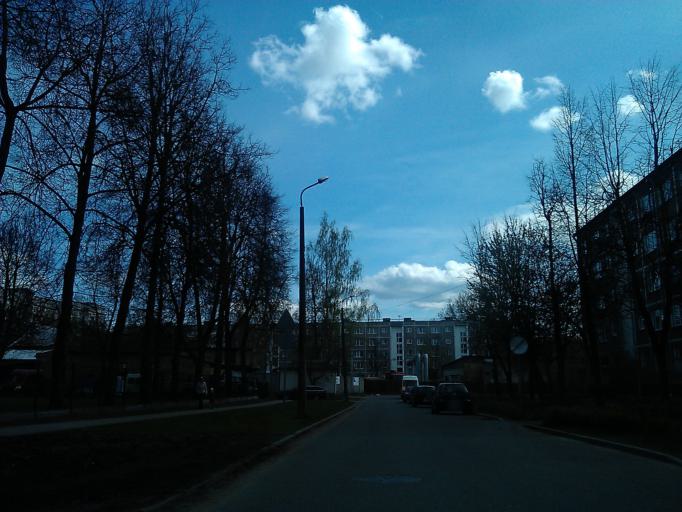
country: LV
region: Kekava
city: Balozi
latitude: 56.9090
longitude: 24.1909
